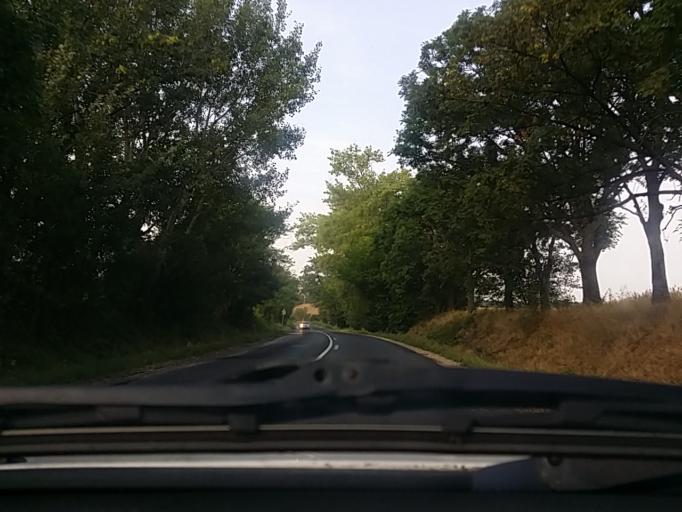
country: HU
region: Fejer
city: Szarliget
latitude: 47.4423
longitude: 18.5418
